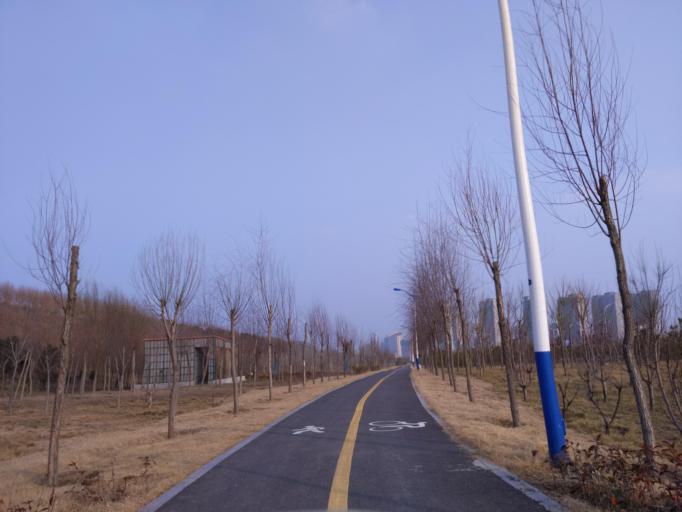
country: CN
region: Henan Sheng
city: Puyang
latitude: 35.8194
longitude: 115.0000
